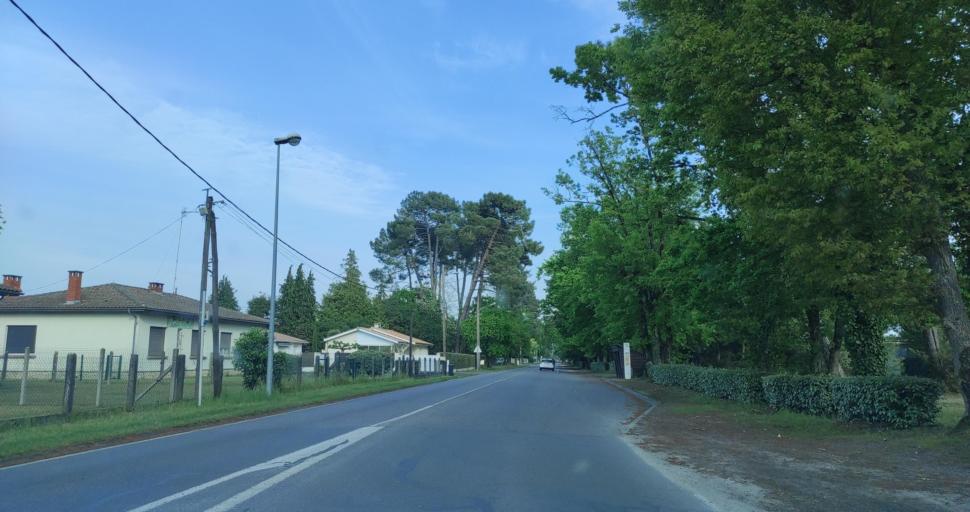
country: FR
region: Aquitaine
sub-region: Departement de la Gironde
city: Ares
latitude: 44.7615
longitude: -1.1287
